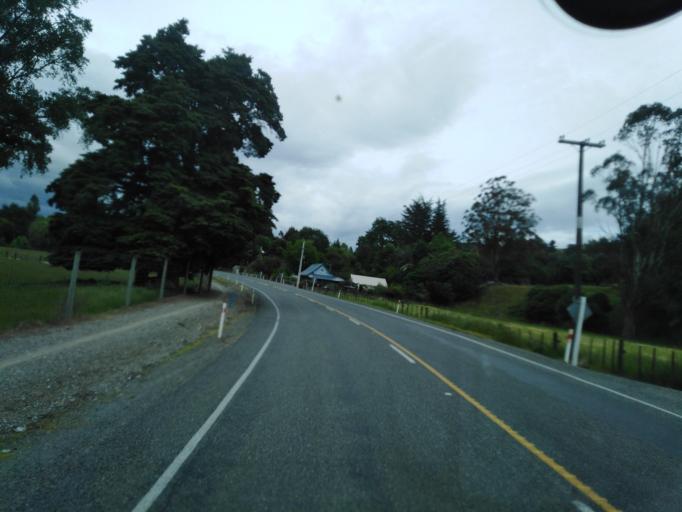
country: NZ
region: Tasman
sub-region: Tasman District
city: Wakefield
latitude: -41.4556
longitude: 172.9548
